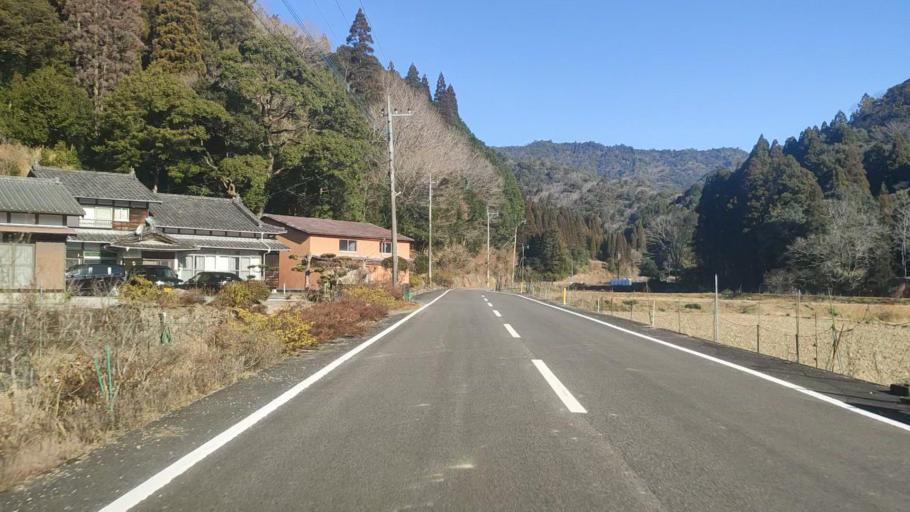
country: JP
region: Oita
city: Saiki
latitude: 32.7764
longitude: 131.8298
